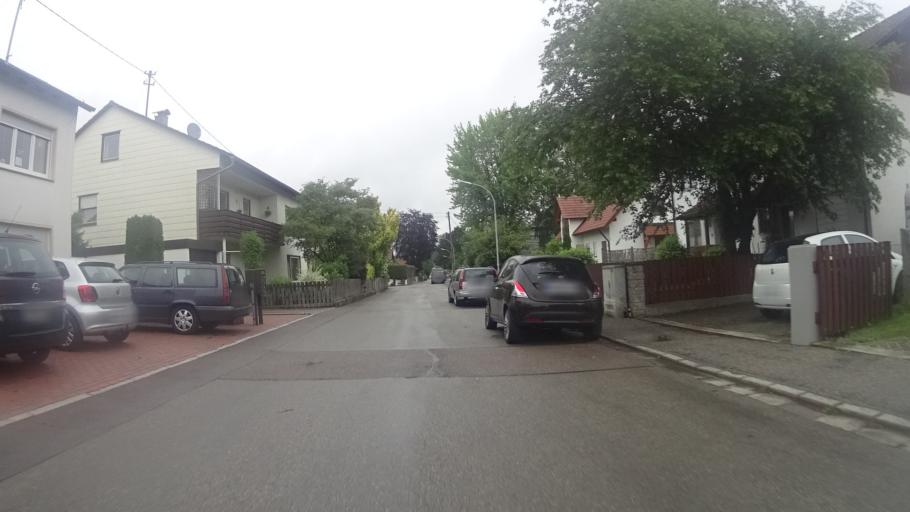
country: DE
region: Bavaria
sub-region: Upper Bavaria
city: Mammendorf
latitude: 48.2119
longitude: 11.1664
